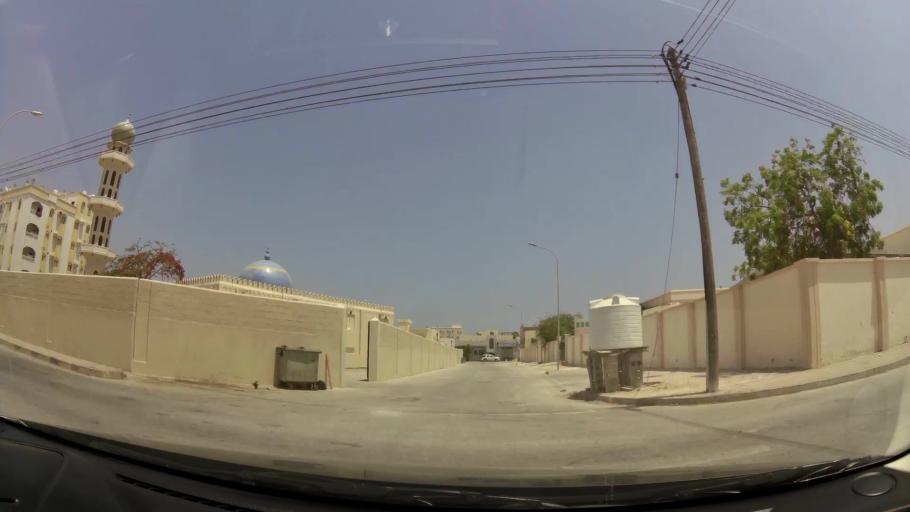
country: OM
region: Zufar
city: Salalah
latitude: 17.0199
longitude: 54.0813
